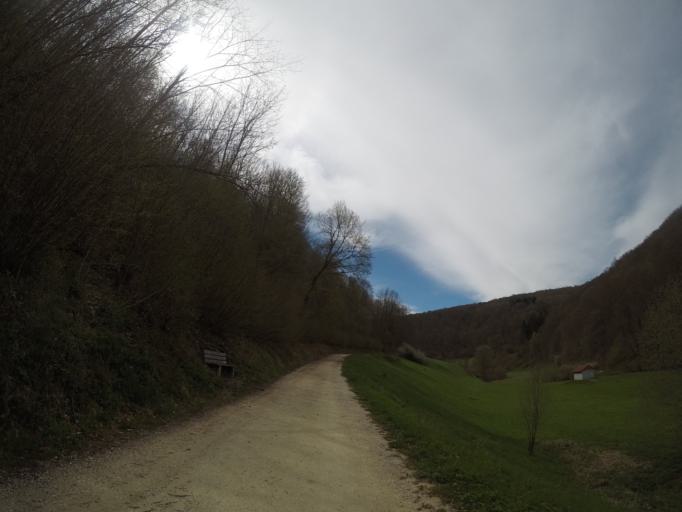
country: DE
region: Baden-Wuerttemberg
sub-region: Regierungsbezirk Stuttgart
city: Wiesensteig
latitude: 48.5590
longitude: 9.6005
